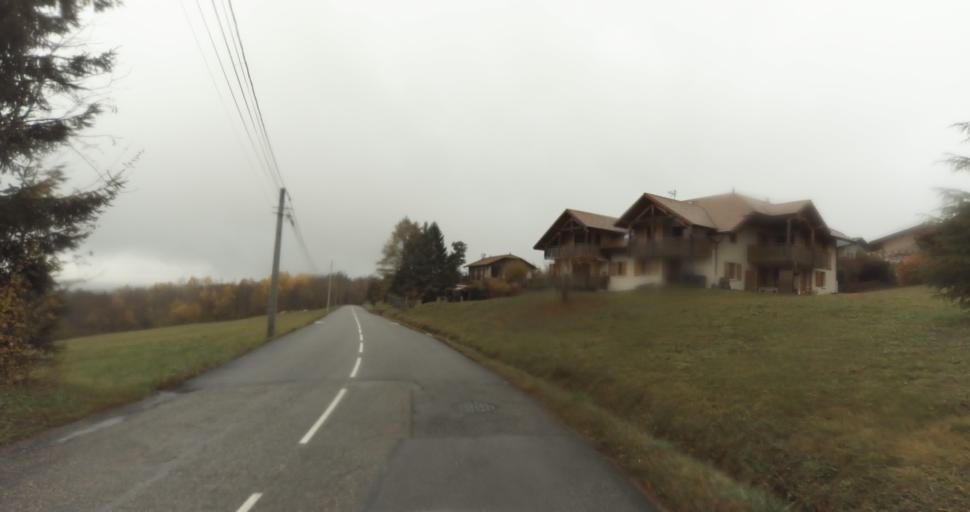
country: FR
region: Rhone-Alpes
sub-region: Departement de la Haute-Savoie
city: Thorens-Glieres
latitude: 45.9828
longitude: 6.2295
